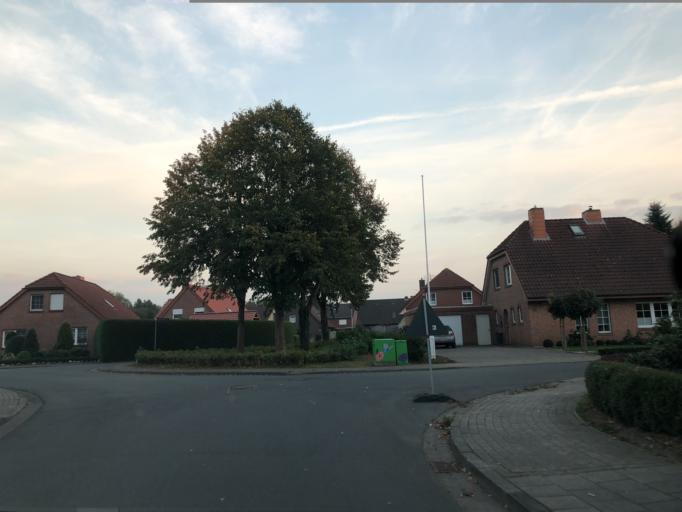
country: DE
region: Lower Saxony
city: Papenburg
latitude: 53.0696
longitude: 7.4321
